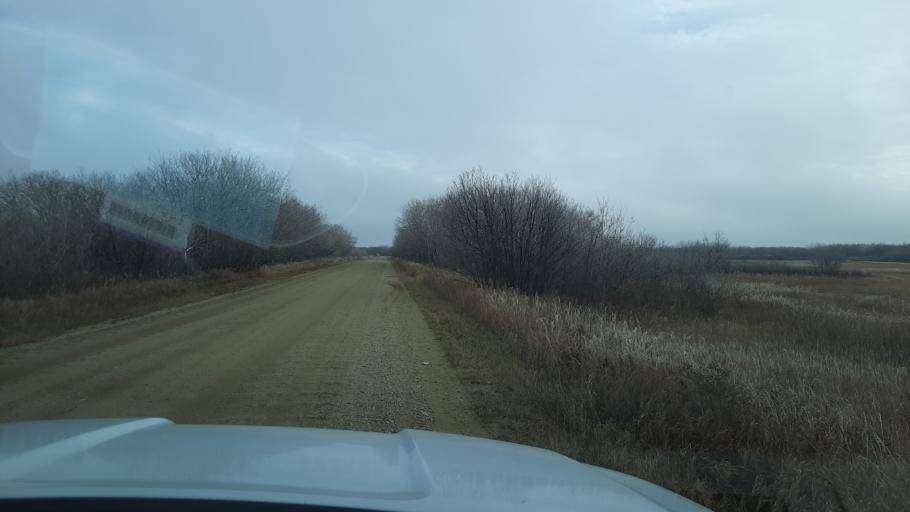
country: CA
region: Saskatchewan
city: White City
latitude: 50.7685
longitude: -104.1185
